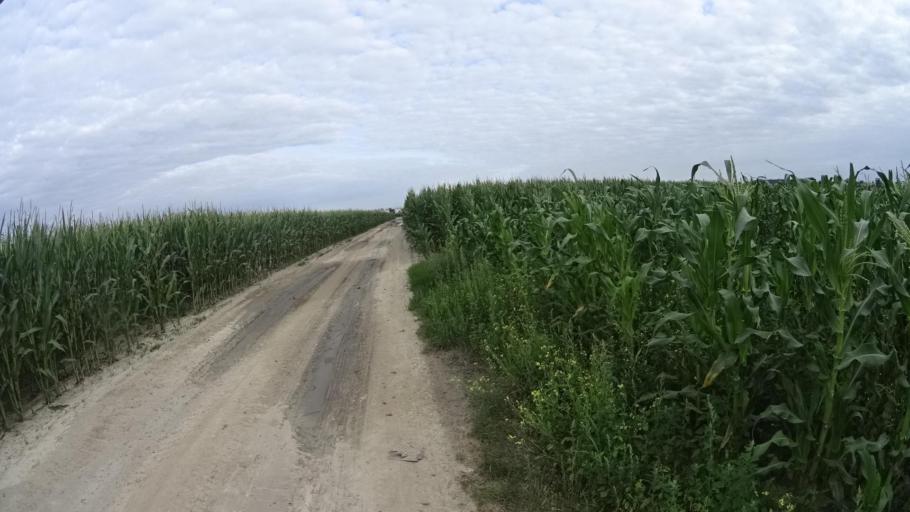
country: PL
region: Masovian Voivodeship
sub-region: Powiat warszawski zachodni
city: Babice
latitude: 52.2348
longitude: 20.8730
